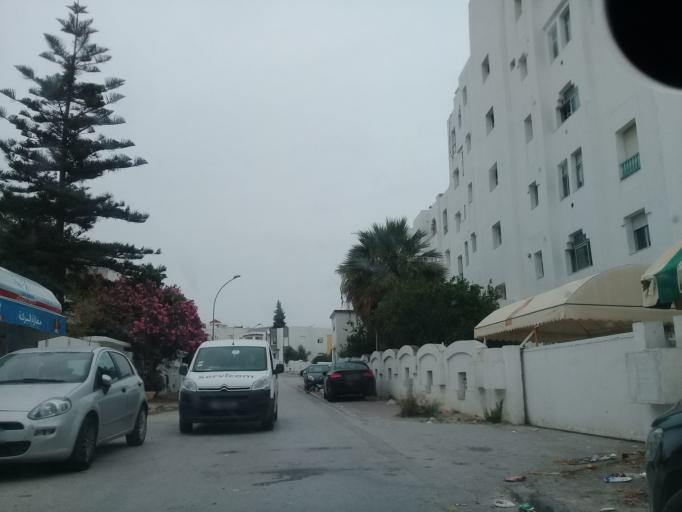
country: TN
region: Tunis
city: Tunis
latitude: 36.8449
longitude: 10.1525
